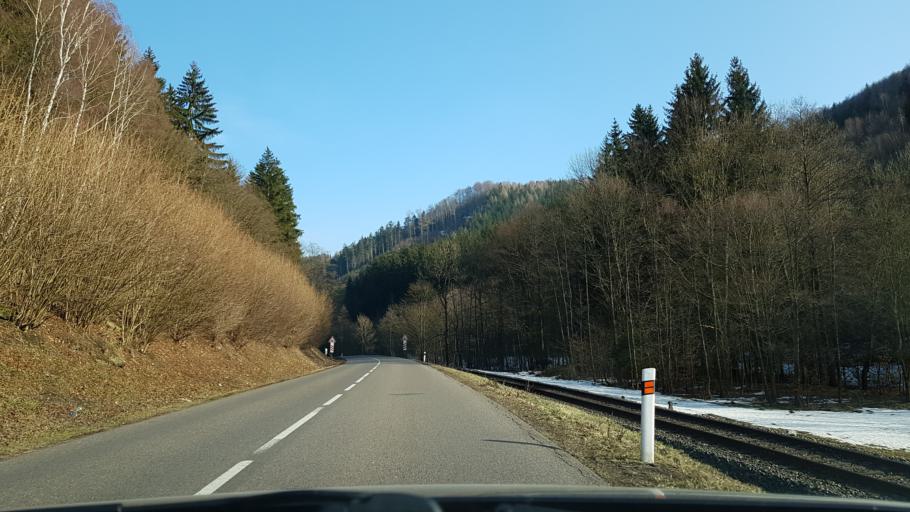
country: CZ
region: Olomoucky
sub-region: Okres Sumperk
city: Hanusovice
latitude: 50.0781
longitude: 16.9488
